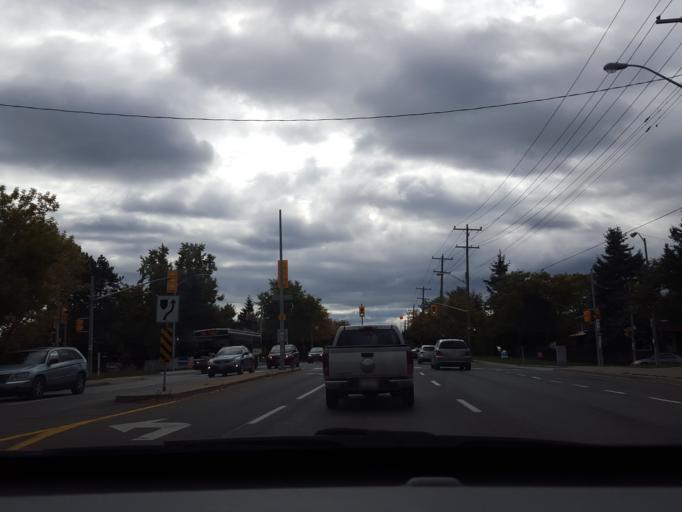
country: CA
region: Ontario
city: Scarborough
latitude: 43.7957
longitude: -79.2938
